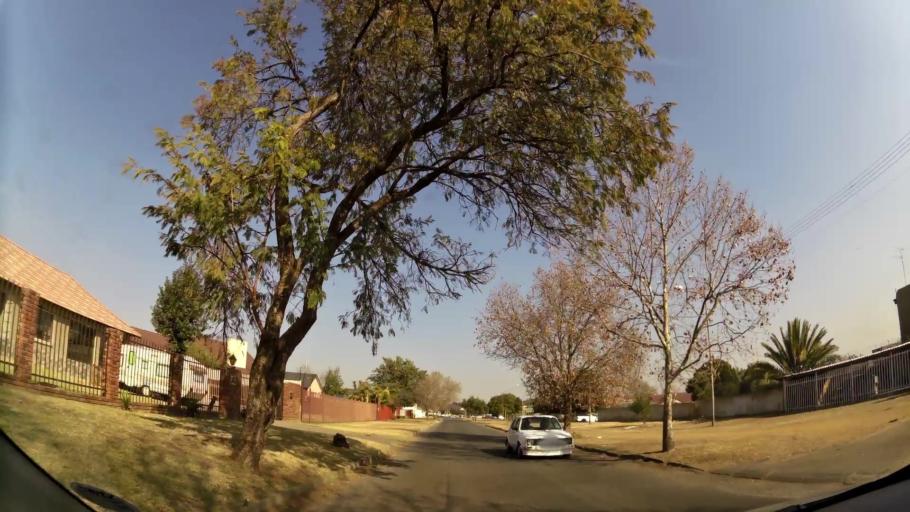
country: ZA
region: Gauteng
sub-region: West Rand District Municipality
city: Randfontein
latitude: -26.1640
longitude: 27.6988
